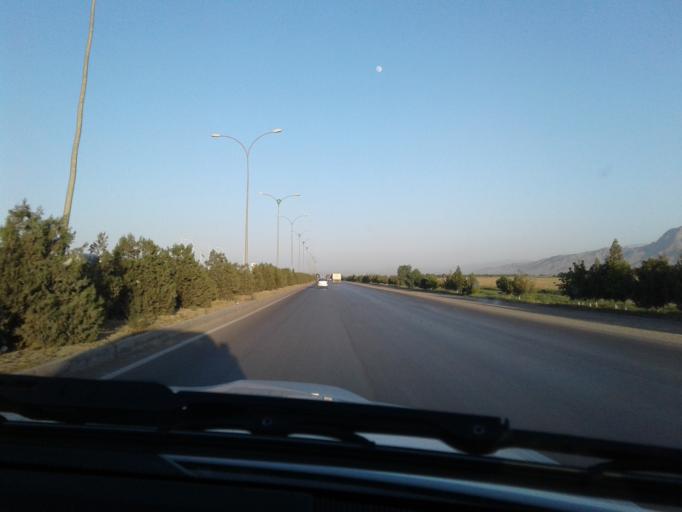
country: TM
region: Ahal
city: Abadan
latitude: 38.1408
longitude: 57.9995
